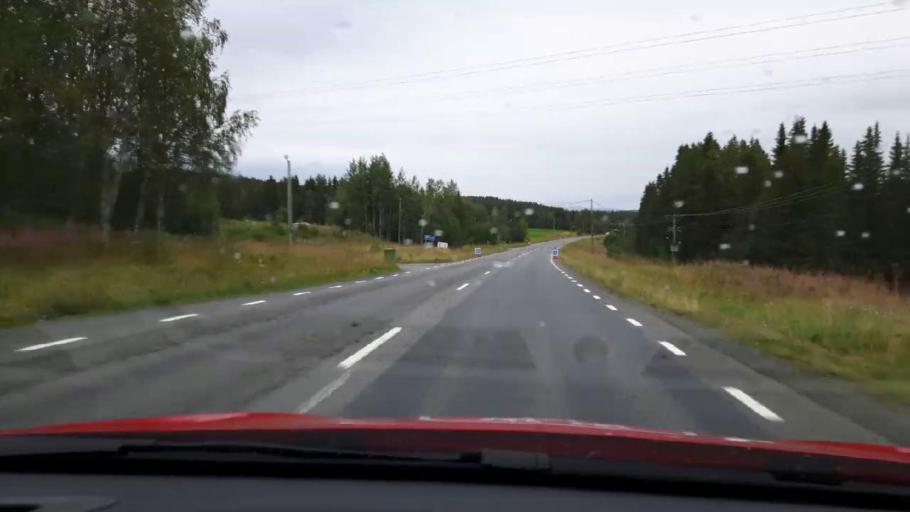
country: SE
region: Jaemtland
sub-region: Are Kommun
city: Jarpen
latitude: 63.3808
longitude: 13.4242
